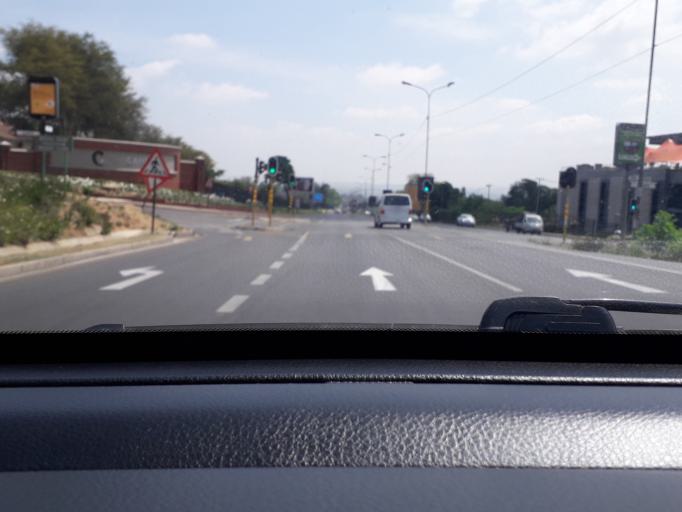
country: ZA
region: Gauteng
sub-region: City of Johannesburg Metropolitan Municipality
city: Diepsloot
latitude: -26.0449
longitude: 28.0250
